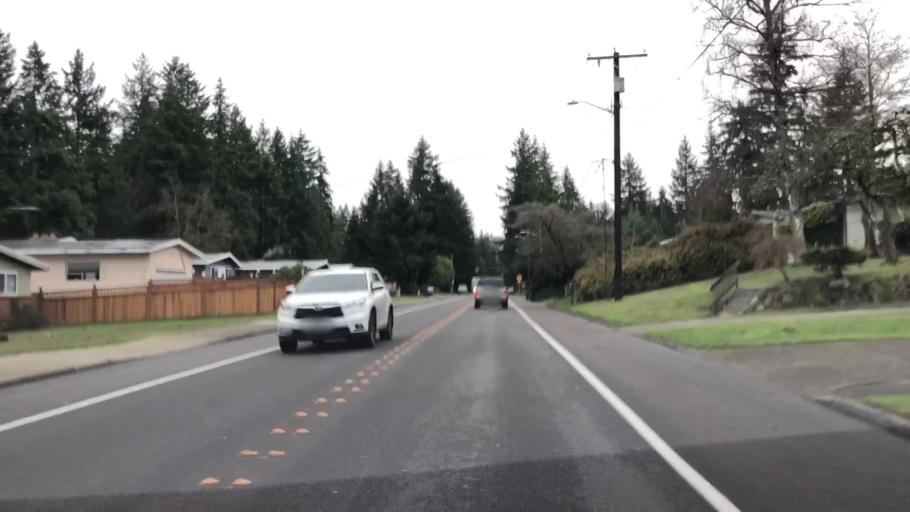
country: US
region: Washington
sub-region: King County
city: Eastgate
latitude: 47.5877
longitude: -122.1325
